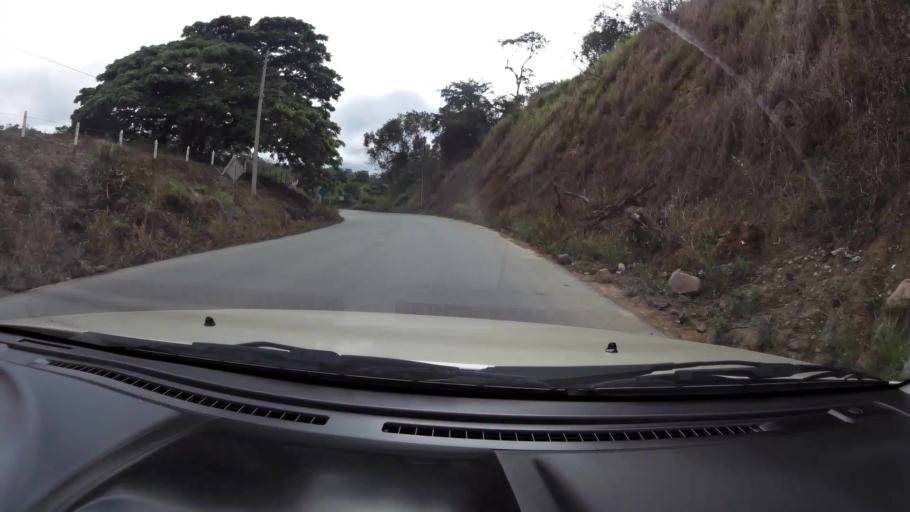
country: EC
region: El Oro
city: Pasaje
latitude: -3.3205
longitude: -79.6716
